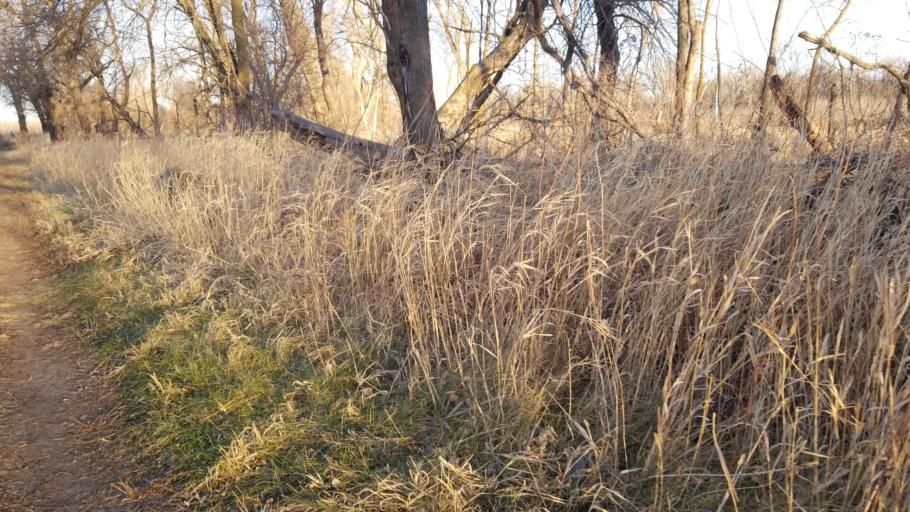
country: US
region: Nebraska
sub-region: Sarpy County
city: Bellevue
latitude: 41.1743
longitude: -95.8829
